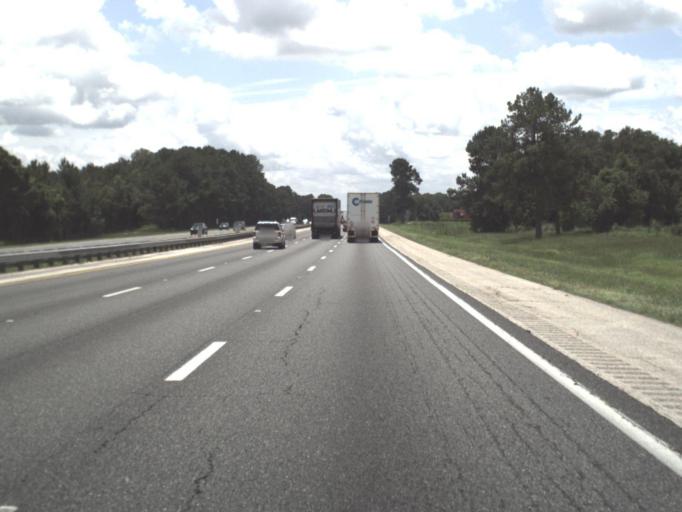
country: US
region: Florida
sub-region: Alachua County
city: High Springs
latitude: 29.8315
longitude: -82.5241
